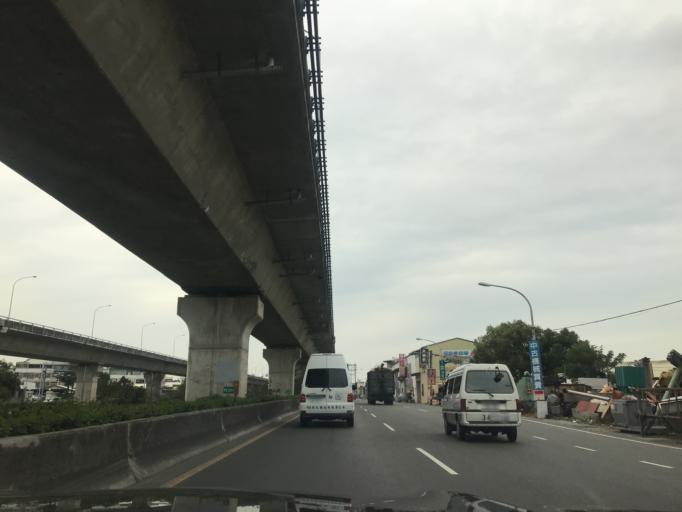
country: TW
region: Taiwan
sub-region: Nantou
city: Nantou
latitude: 23.9467
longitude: 120.5614
